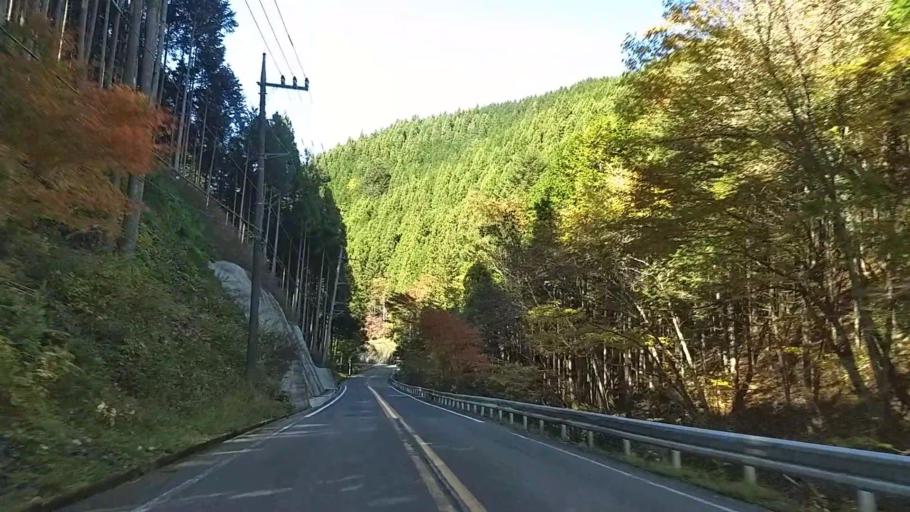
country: JP
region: Yamanashi
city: Otsuki
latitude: 35.7354
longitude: 138.9722
